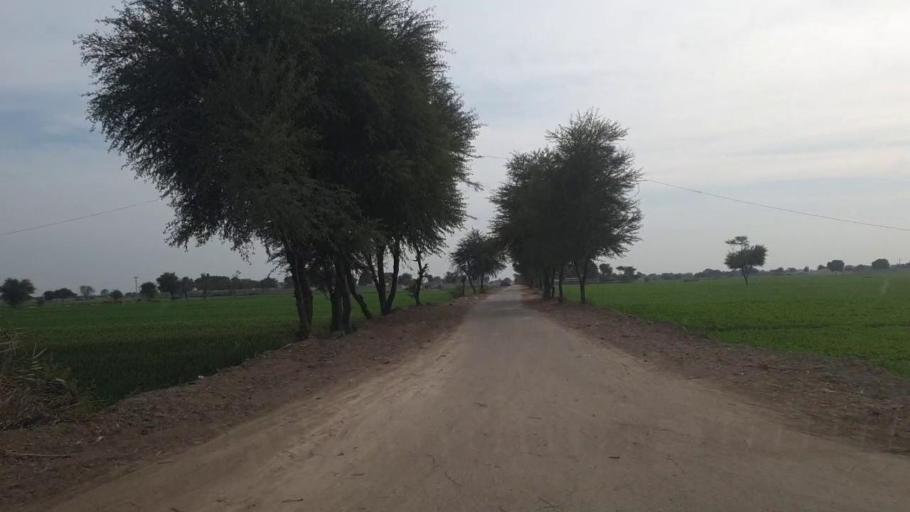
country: PK
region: Sindh
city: Shahpur Chakar
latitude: 26.1071
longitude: 68.5232
